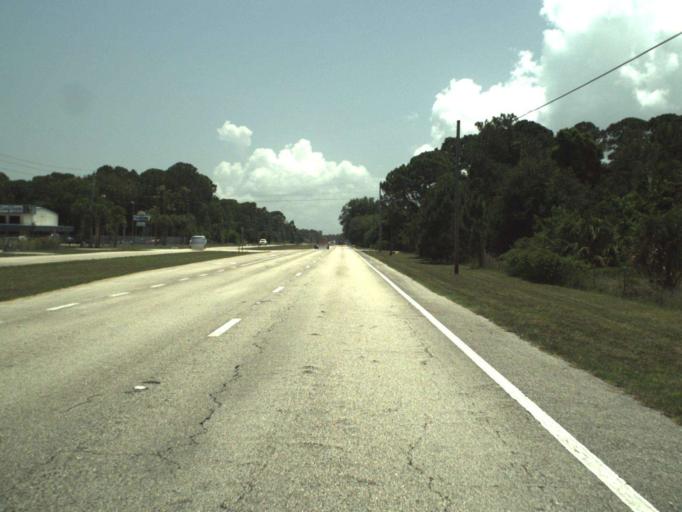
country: US
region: Florida
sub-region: Volusia County
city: Oak Hill
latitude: 28.9096
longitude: -80.8670
